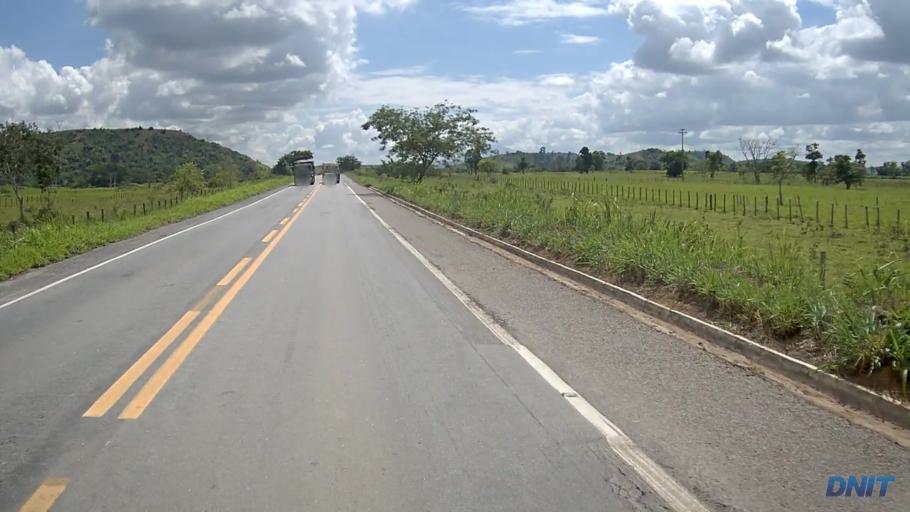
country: BR
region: Minas Gerais
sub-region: Governador Valadares
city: Governador Valadares
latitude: -19.0042
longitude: -42.1295
